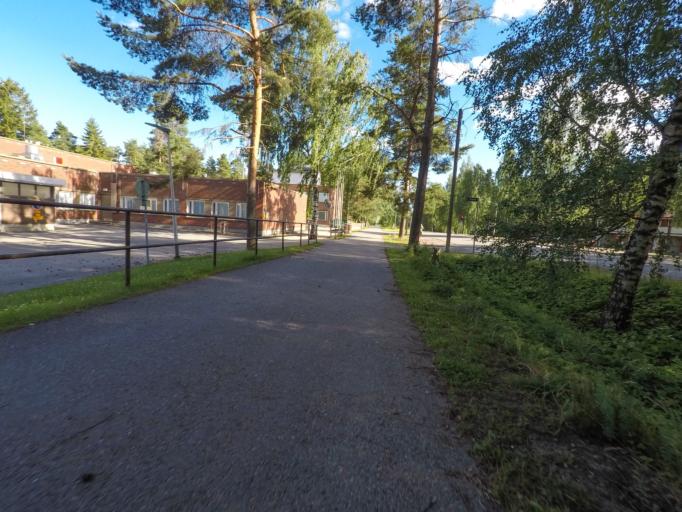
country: FI
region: South Karelia
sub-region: Lappeenranta
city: Lappeenranta
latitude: 61.0819
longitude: 28.1486
